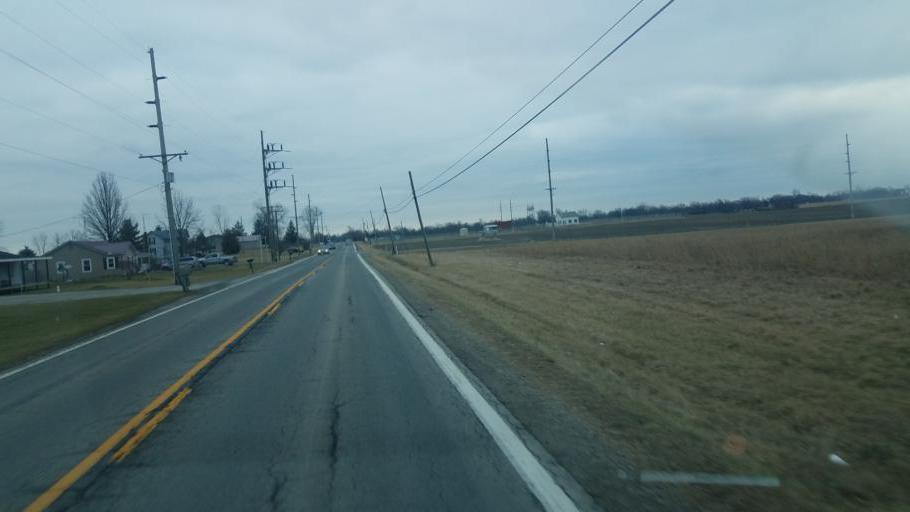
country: US
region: Ohio
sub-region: Marion County
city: Marion
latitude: 40.6126
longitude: -83.2041
